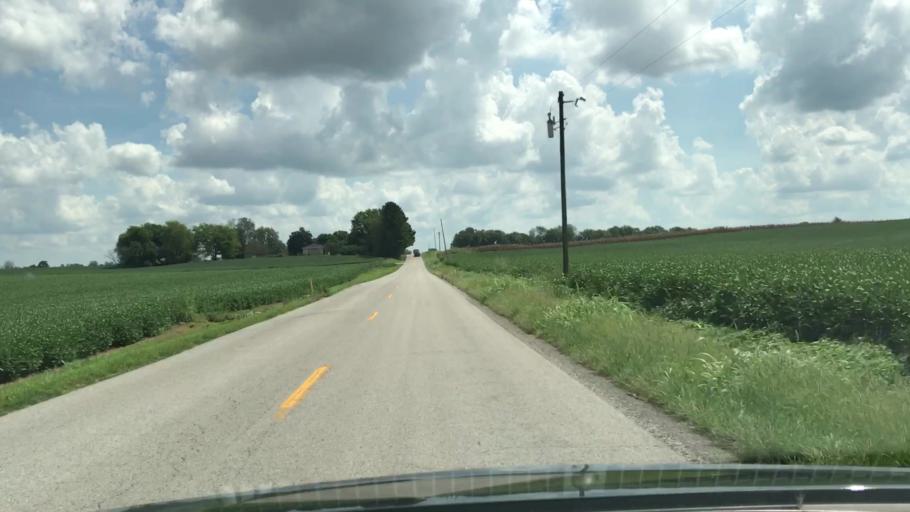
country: US
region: Kentucky
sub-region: Todd County
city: Guthrie
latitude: 36.7129
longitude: -87.0596
